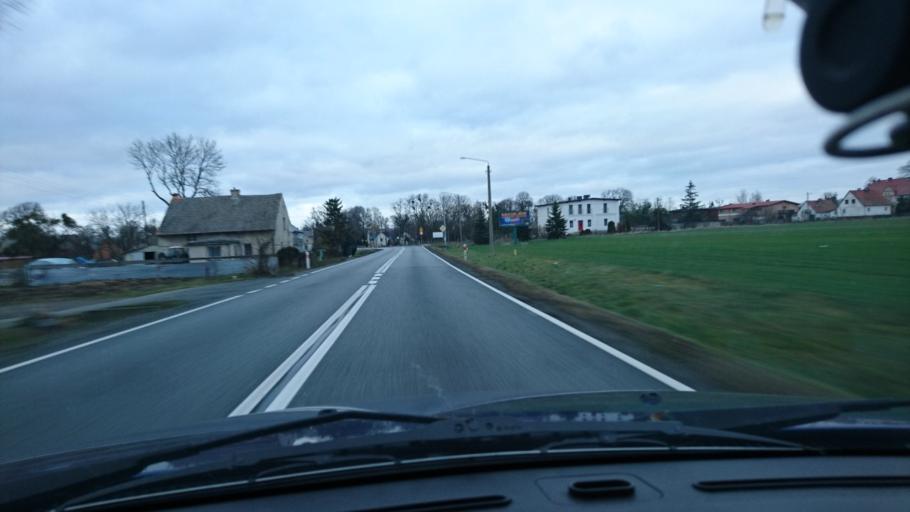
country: PL
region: Opole Voivodeship
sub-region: Powiat kluczborski
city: Byczyna
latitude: 51.0601
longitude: 18.1996
